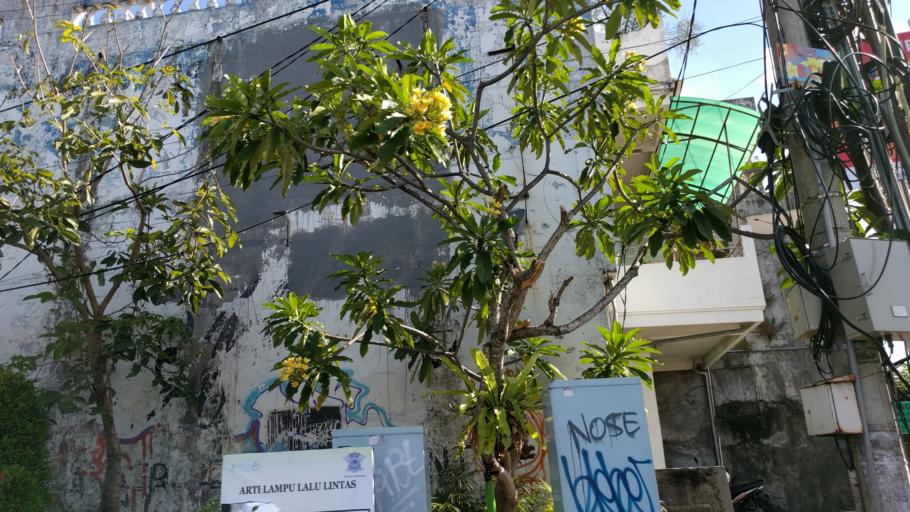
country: ID
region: Bali
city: Kuta
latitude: -8.7057
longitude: 115.1828
